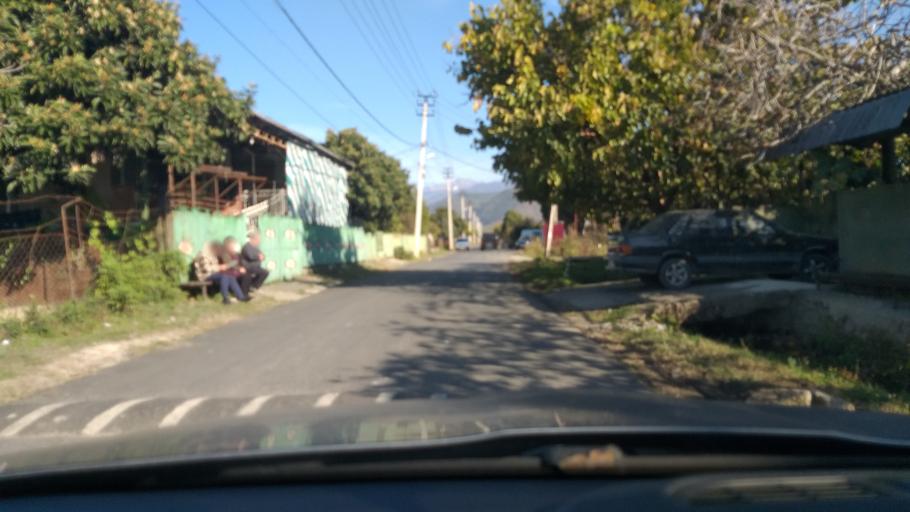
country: GE
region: Abkhazia
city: Sokhumi
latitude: 43.0181
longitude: 40.9662
